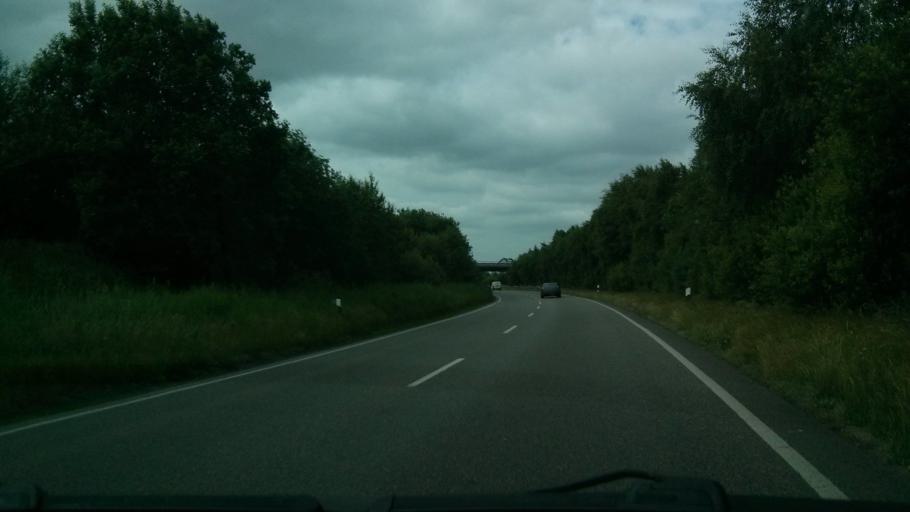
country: DE
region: Lower Saxony
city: Driftsethe
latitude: 53.4395
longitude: 8.5733
